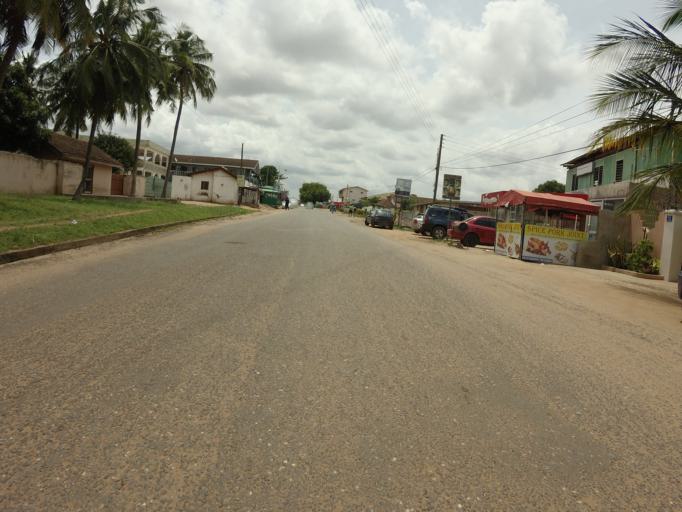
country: GH
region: Greater Accra
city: Dome
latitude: 5.6231
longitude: -0.2426
